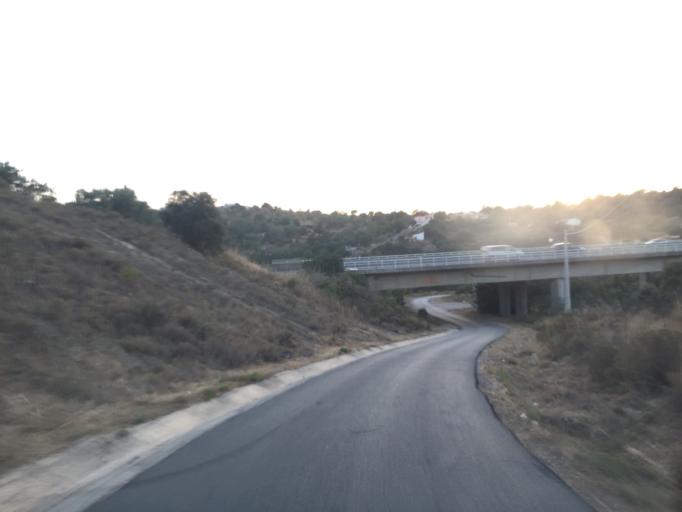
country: PT
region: Faro
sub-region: Loule
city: Almancil
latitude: 37.1034
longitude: -8.0136
